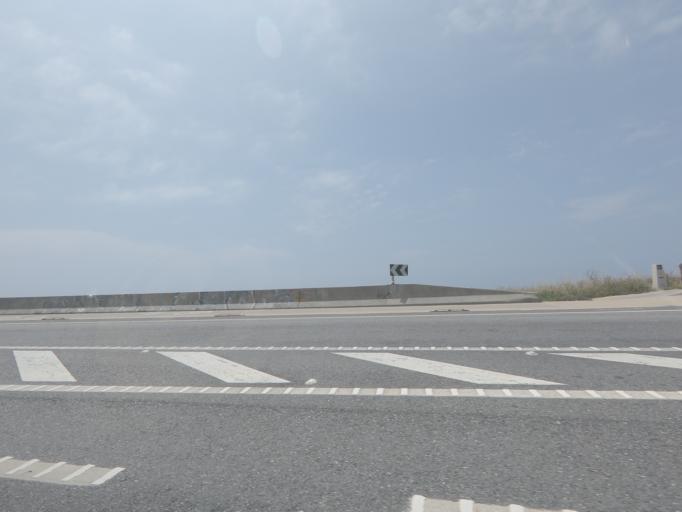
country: ES
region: Galicia
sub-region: Provincia de Pontevedra
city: A Guarda
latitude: 41.9372
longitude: -8.8849
